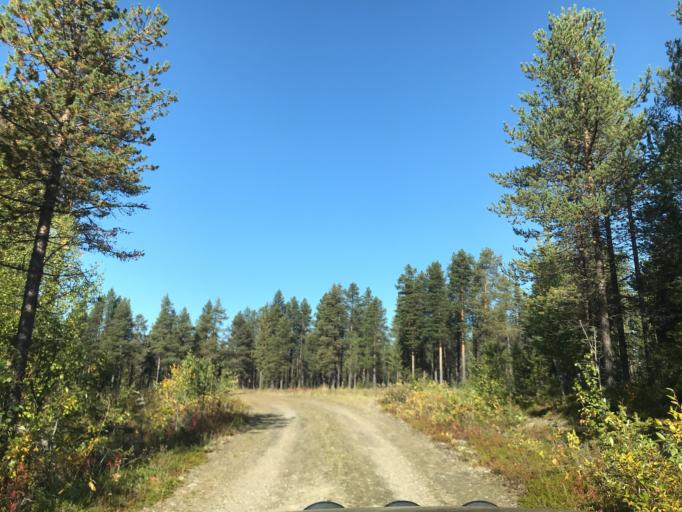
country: SE
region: Norrbotten
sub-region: Gallivare Kommun
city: Malmberget
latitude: 67.6493
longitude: 21.0824
